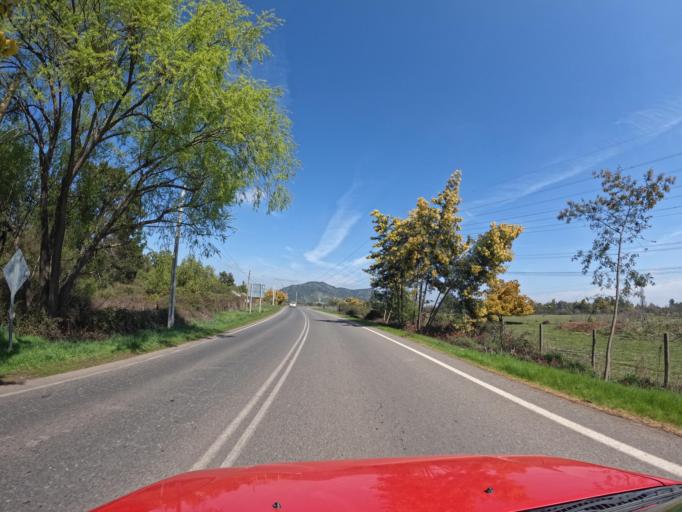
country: CL
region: Maule
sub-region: Provincia de Talca
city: San Clemente
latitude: -35.4869
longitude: -71.2843
